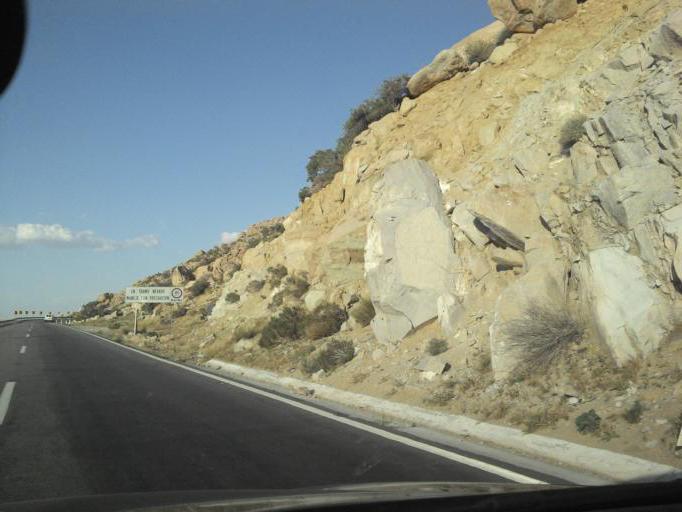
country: MX
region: Baja California
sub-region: Tecate
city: Cereso del Hongo
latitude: 32.5786
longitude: -116.0311
